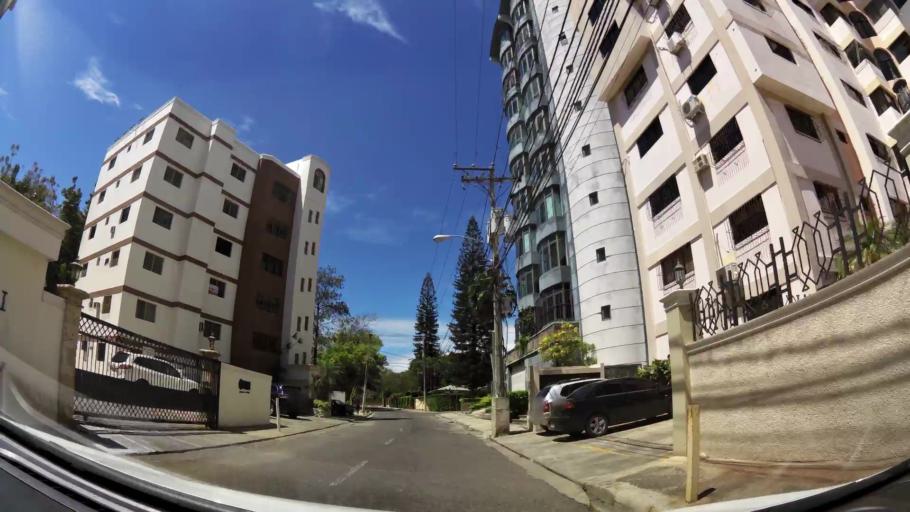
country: DO
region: Santiago
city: Santiago de los Caballeros
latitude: 19.4546
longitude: -70.6896
